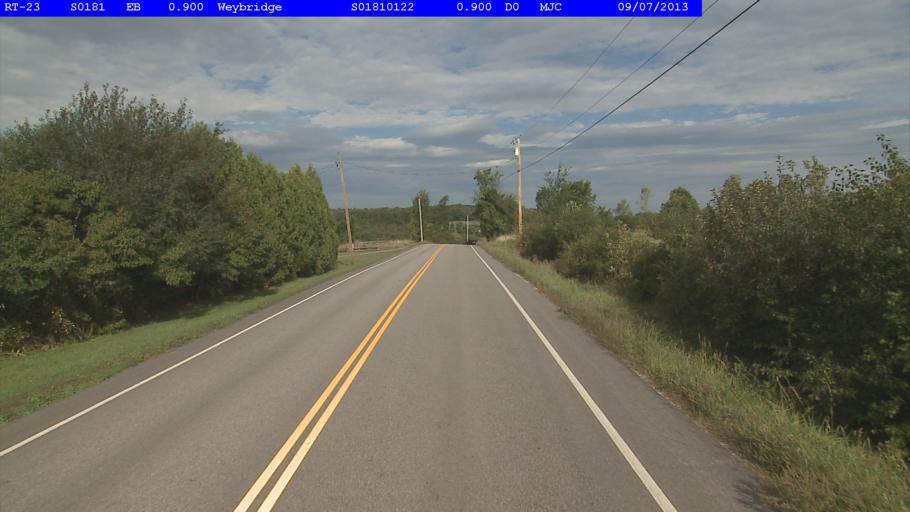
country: US
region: Vermont
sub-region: Addison County
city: Middlebury (village)
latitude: 44.0269
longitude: -73.1967
